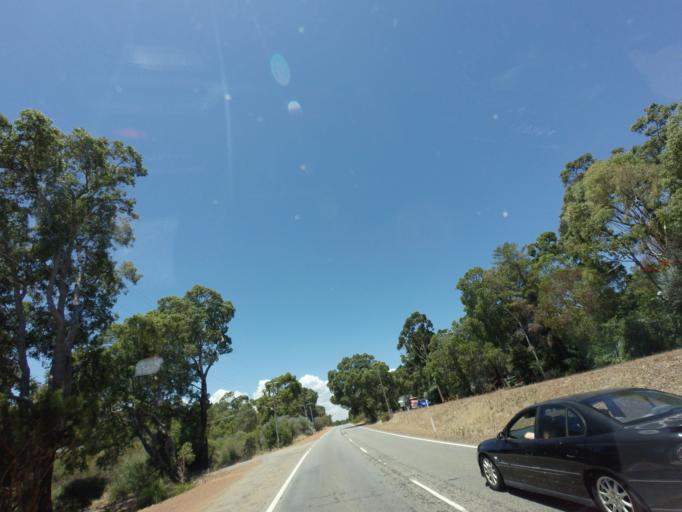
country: AU
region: Western Australia
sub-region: Mundaring
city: Parkerville
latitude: -31.8992
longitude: 116.1198
